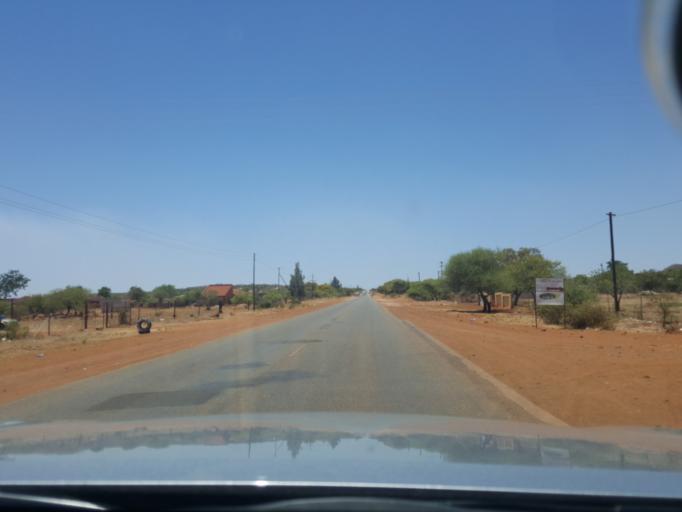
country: ZA
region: North-West
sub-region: Ngaka Modiri Molema District Municipality
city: Zeerust
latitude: -25.4449
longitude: 25.9651
